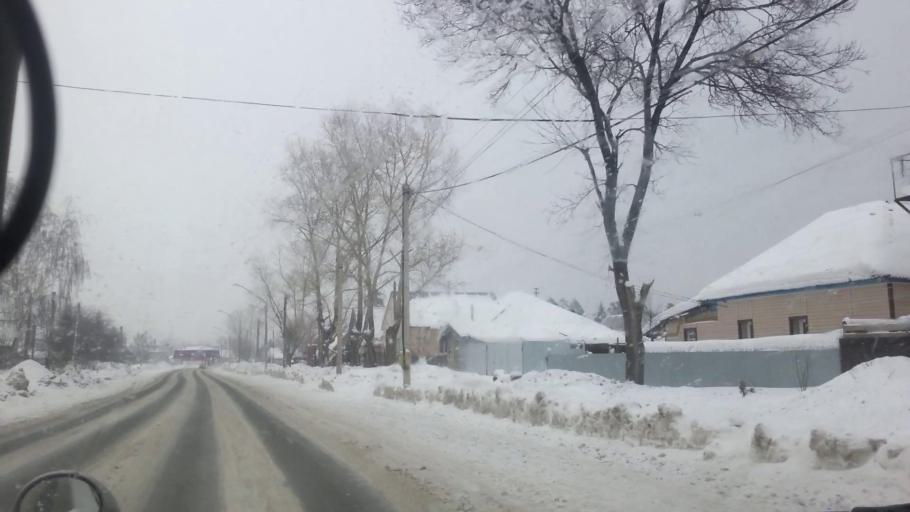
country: RU
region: Altai Krai
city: Vlasikha
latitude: 53.2922
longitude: 83.5686
